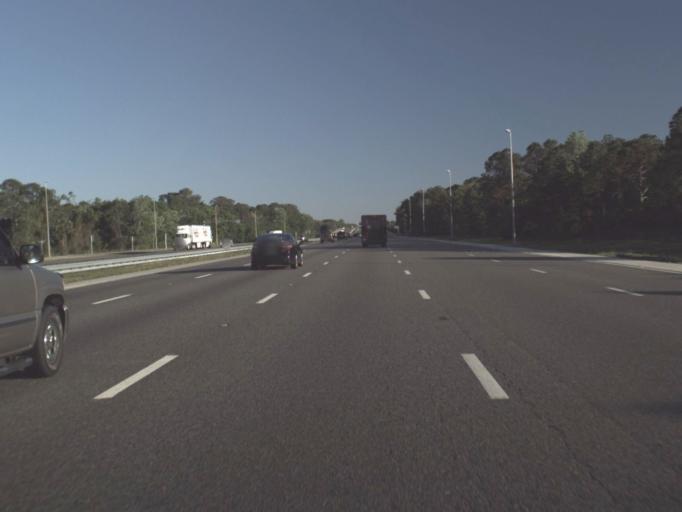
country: US
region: Florida
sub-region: Flagler County
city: Bunnell
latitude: 29.5065
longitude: -81.1956
